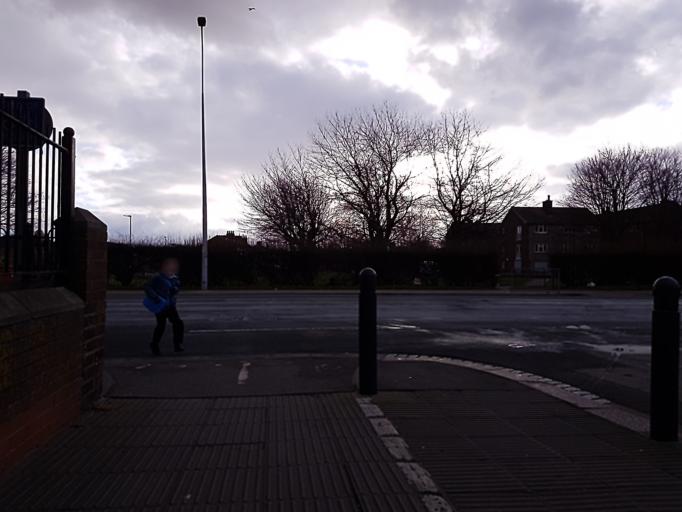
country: GB
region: England
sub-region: North East Lincolnshire
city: Grimsby
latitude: 53.5731
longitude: -0.0663
